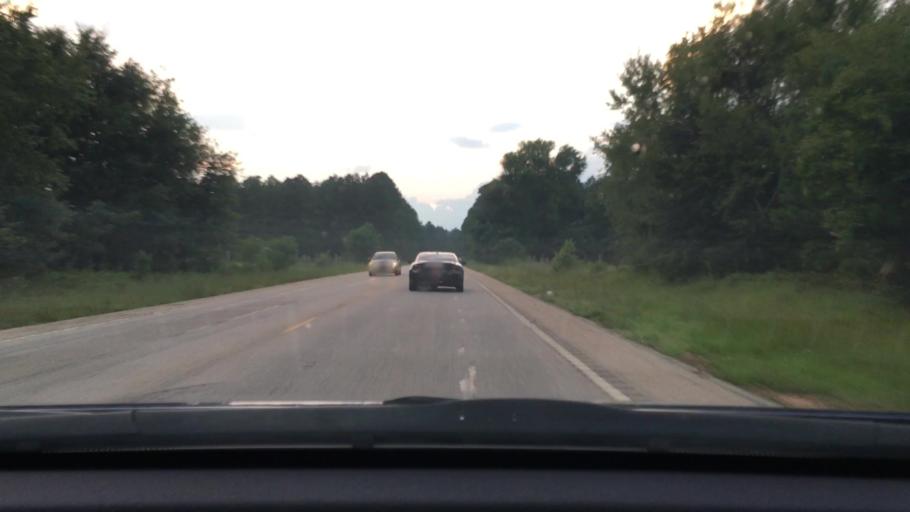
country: US
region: South Carolina
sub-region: Sumter County
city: Cherryvale
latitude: 33.9414
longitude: -80.4848
